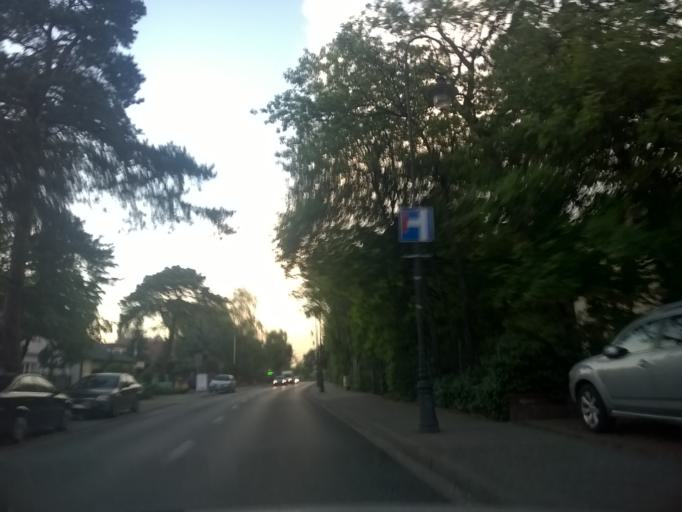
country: PL
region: Masovian Voivodeship
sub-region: Powiat piaseczynski
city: Konstancin-Jeziorna
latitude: 52.0868
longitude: 21.1208
